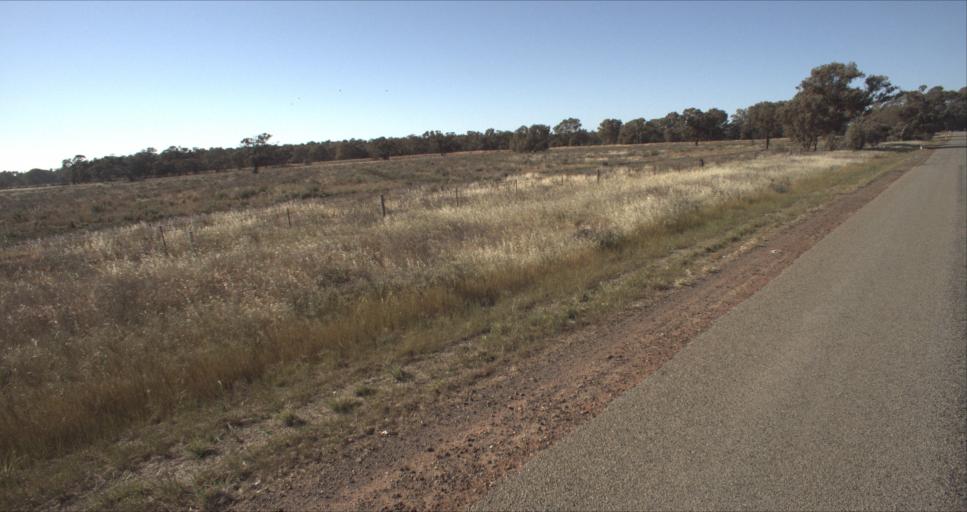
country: AU
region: New South Wales
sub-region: Leeton
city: Leeton
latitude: -34.6016
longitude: 146.2576
